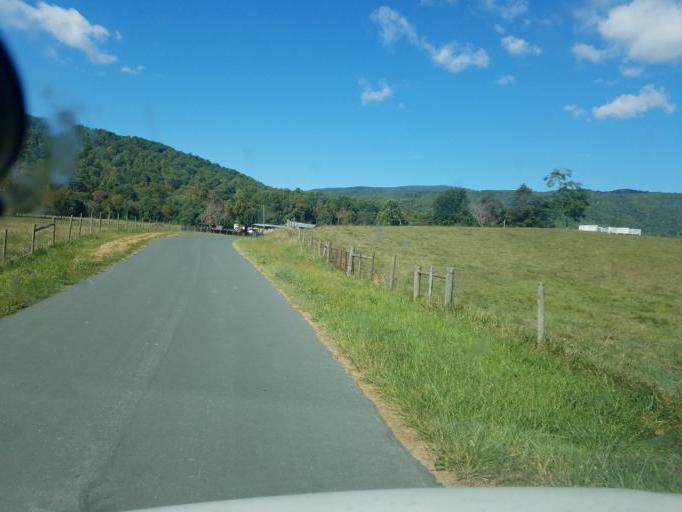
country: US
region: Virginia
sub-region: Greene County
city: Stanardsville
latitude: 38.3652
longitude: -78.4243
